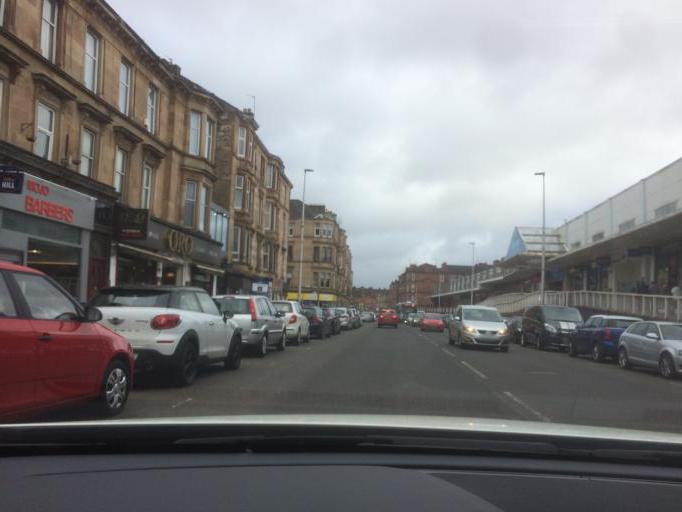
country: GB
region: Scotland
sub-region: East Renfrewshire
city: Giffnock
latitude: 55.8288
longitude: -4.2831
